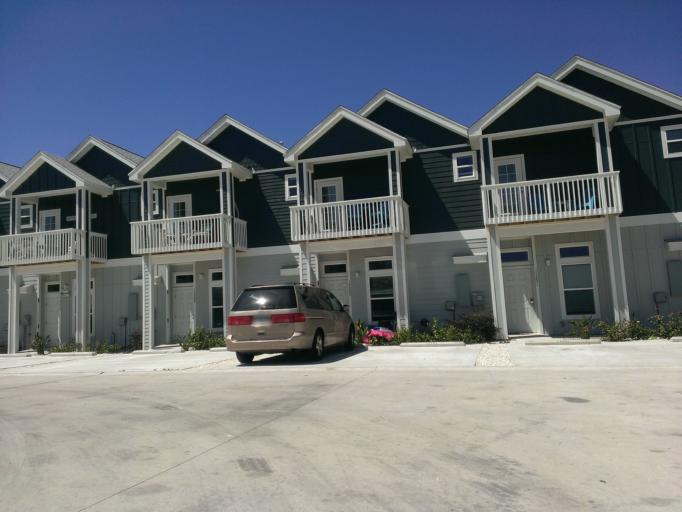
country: US
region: Texas
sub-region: Nueces County
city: Corpus Christi
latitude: 27.6044
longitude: -97.2108
